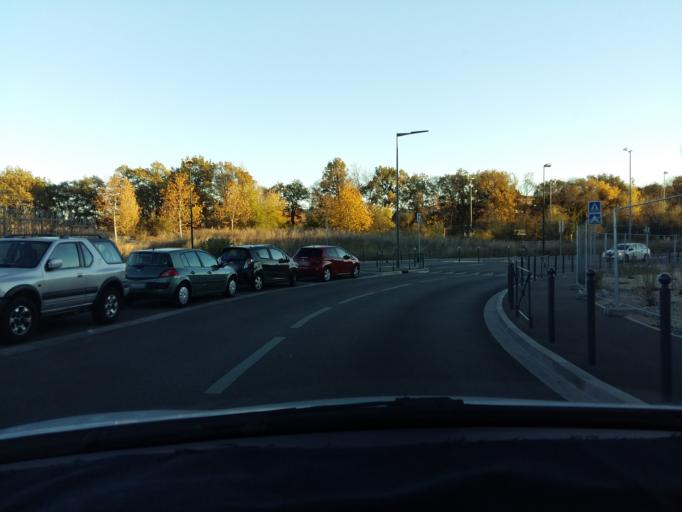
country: FR
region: Provence-Alpes-Cote d'Azur
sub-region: Departement des Bouches-du-Rhone
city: Cabries
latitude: 43.4934
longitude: 5.3557
